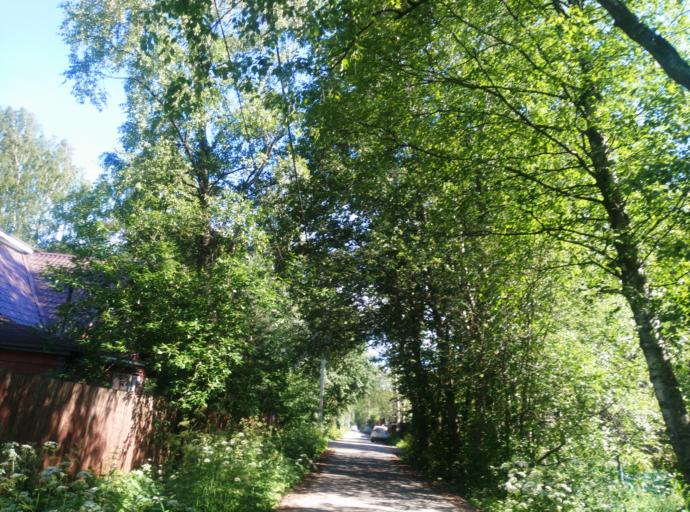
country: RU
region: St.-Petersburg
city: Ozerki
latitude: 60.0324
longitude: 30.3069
